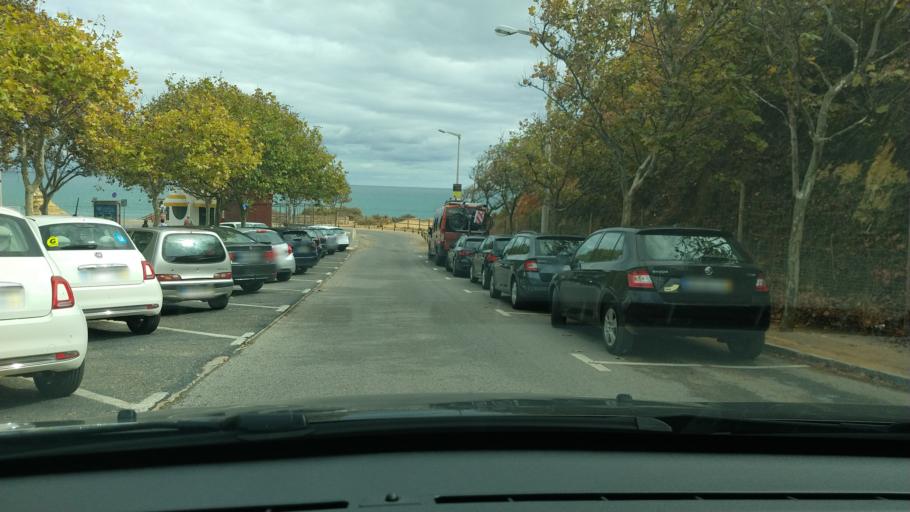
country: PT
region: Faro
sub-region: Lagos
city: Lagos
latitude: 37.0913
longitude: -8.6706
